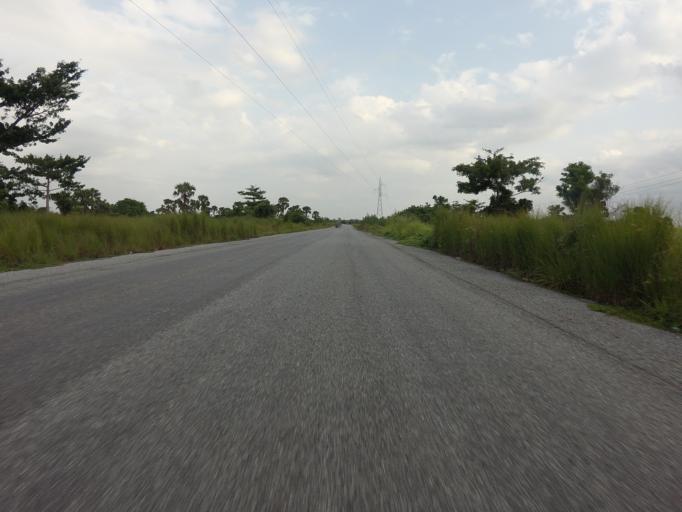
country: GH
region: Volta
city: Ho
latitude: 6.3903
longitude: 0.5269
